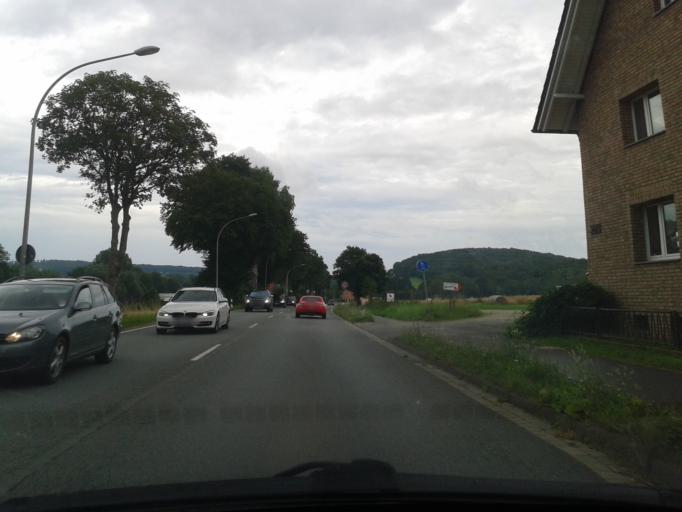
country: DE
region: North Rhine-Westphalia
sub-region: Regierungsbezirk Detmold
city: Horn
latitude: 51.9104
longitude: 8.9185
